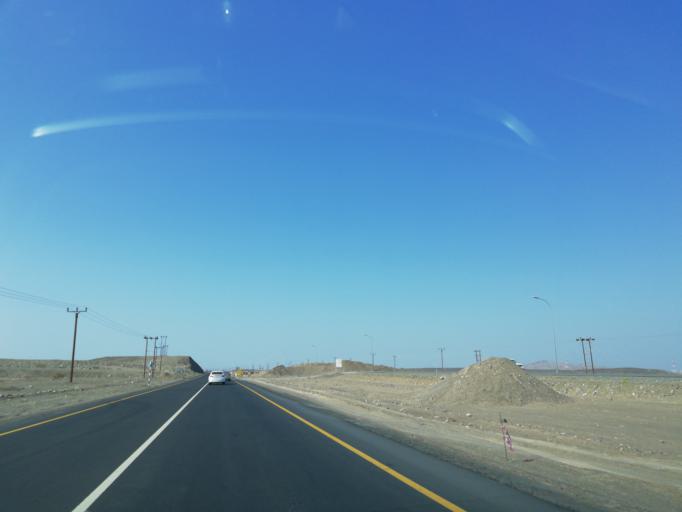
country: OM
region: Ash Sharqiyah
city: Ibra'
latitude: 22.7011
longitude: 58.1404
